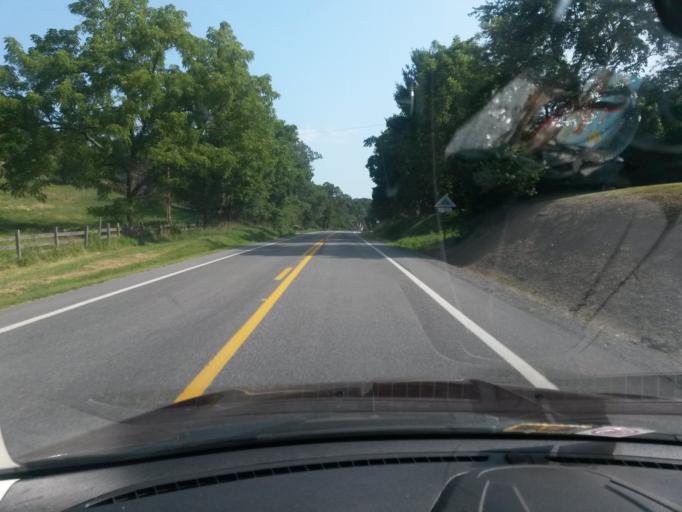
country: US
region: Virginia
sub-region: Shenandoah County
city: Basye
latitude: 38.8174
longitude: -78.8838
